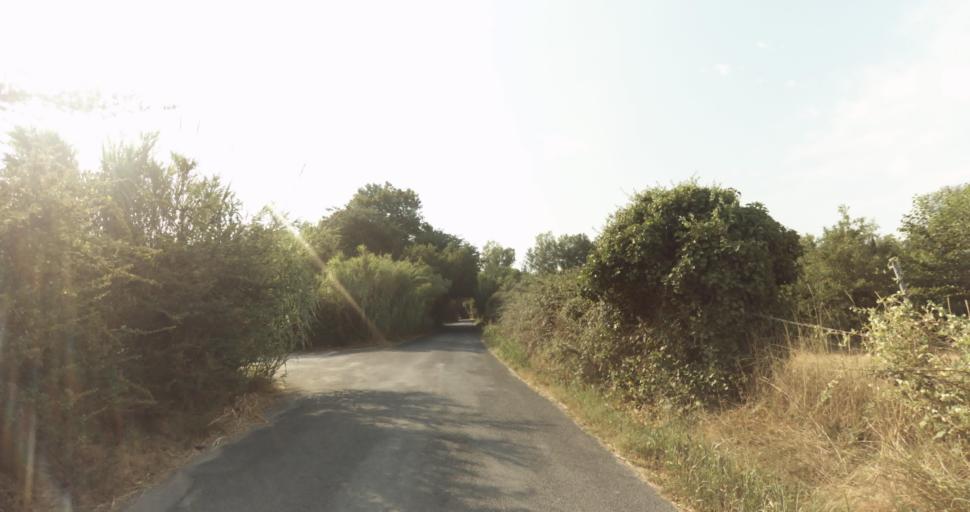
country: FR
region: Languedoc-Roussillon
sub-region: Departement des Pyrenees-Orientales
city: Latour-Bas-Elne
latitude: 42.6165
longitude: 2.9842
